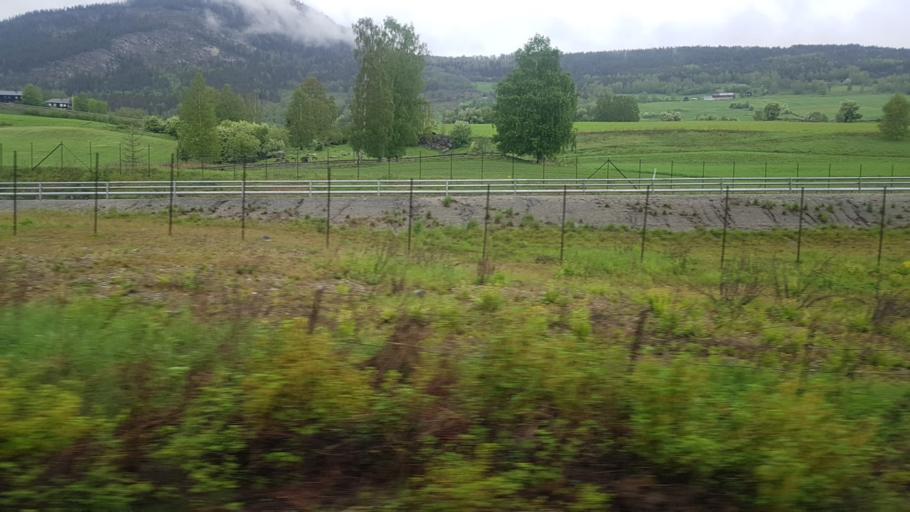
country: NO
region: Oppland
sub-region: Sor-Fron
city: Hundorp
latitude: 61.5715
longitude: 9.8638
